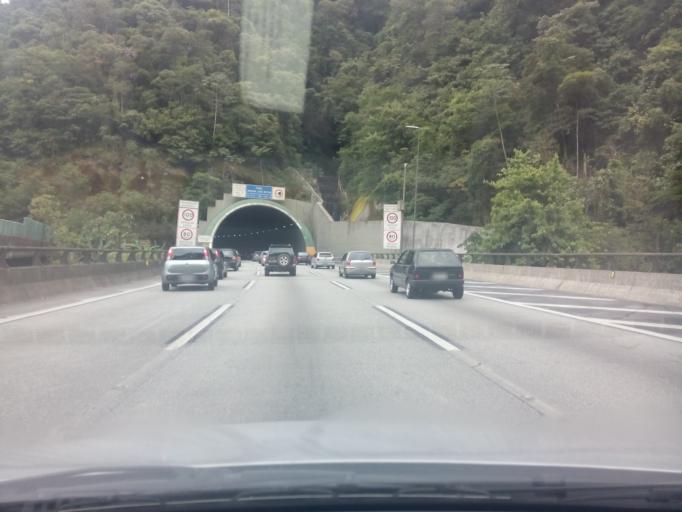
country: BR
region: Sao Paulo
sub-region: Cubatao
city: Cubatao
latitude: -23.8865
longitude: -46.5002
